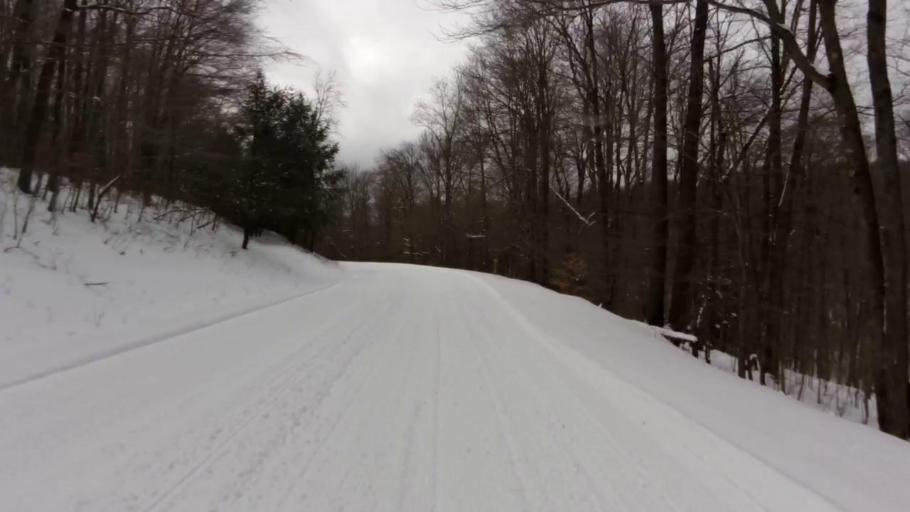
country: US
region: New York
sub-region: Cattaraugus County
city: Salamanca
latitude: 42.0394
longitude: -78.7853
